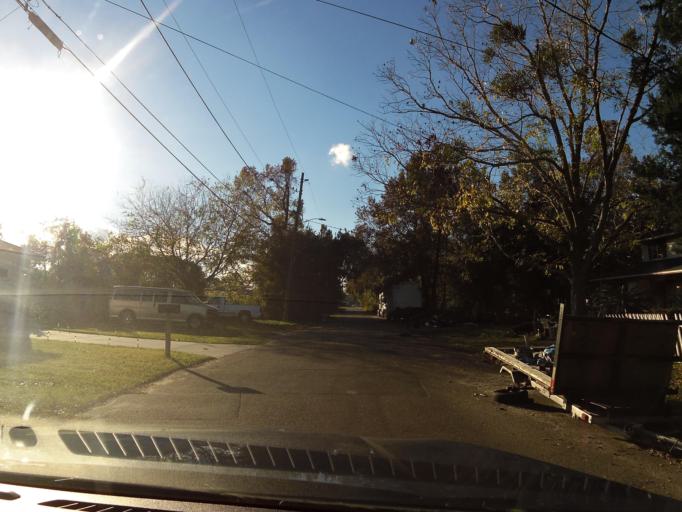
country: US
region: Florida
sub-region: Duval County
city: Jacksonville
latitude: 30.3398
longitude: -81.7030
